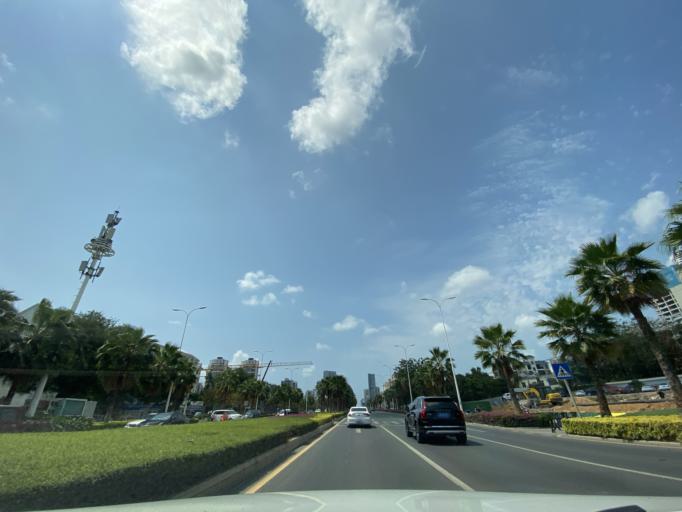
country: CN
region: Hainan
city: Sanya
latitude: 18.2847
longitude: 109.5178
